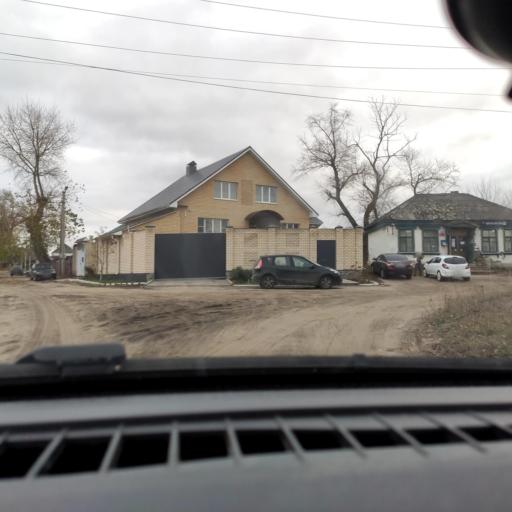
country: RU
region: Voronezj
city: Podgornoye
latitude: 51.7346
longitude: 39.1420
